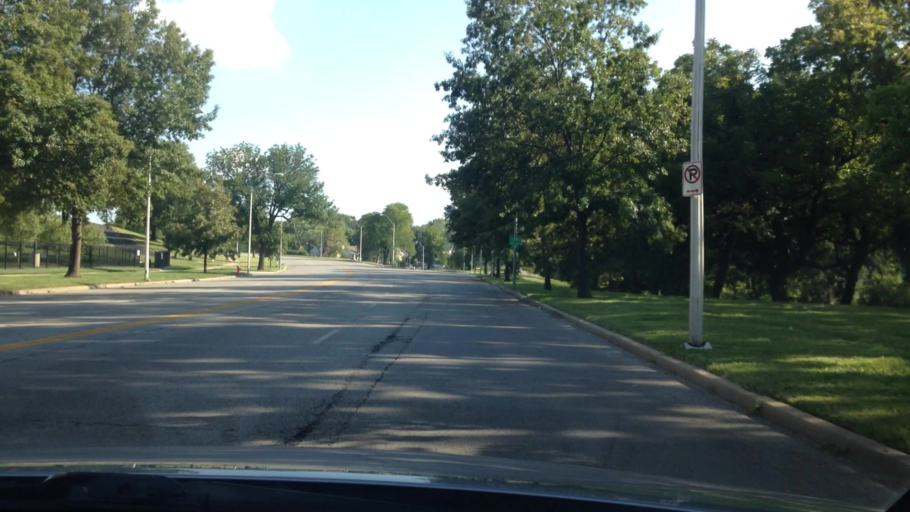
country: US
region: Kansas
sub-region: Johnson County
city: Mission Hills
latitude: 39.0114
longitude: -94.5681
